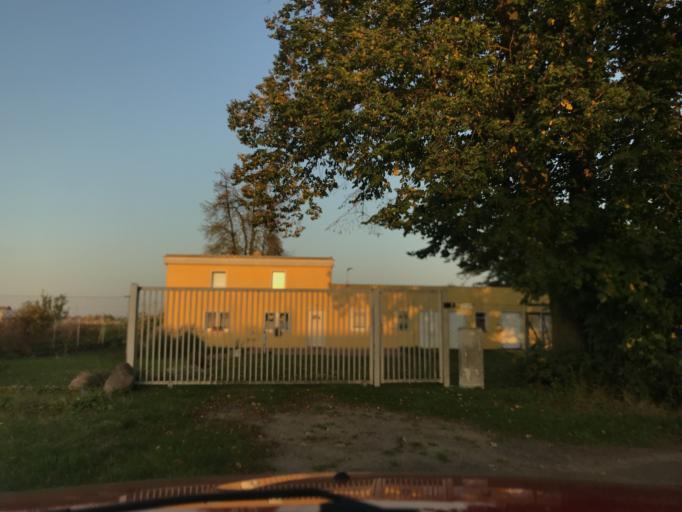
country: PL
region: Greater Poland Voivodeship
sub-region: Powiat poznanski
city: Dopiewo
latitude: 52.3932
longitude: 16.7273
